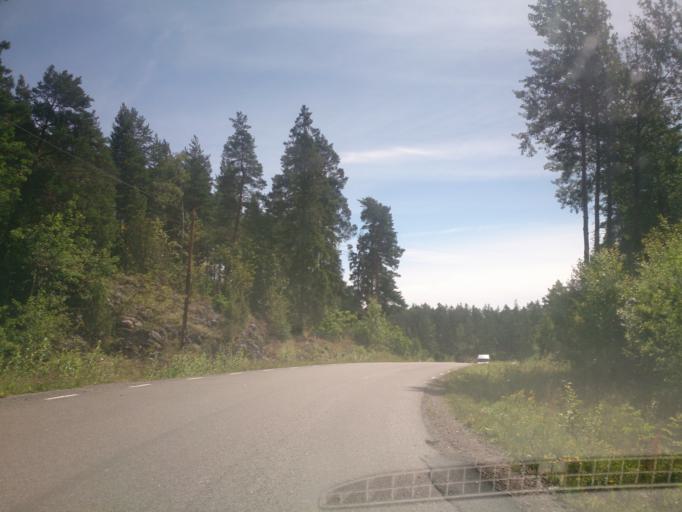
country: SE
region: OEstergoetland
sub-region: Valdemarsviks Kommun
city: Valdemarsvik
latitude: 58.3241
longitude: 16.6440
